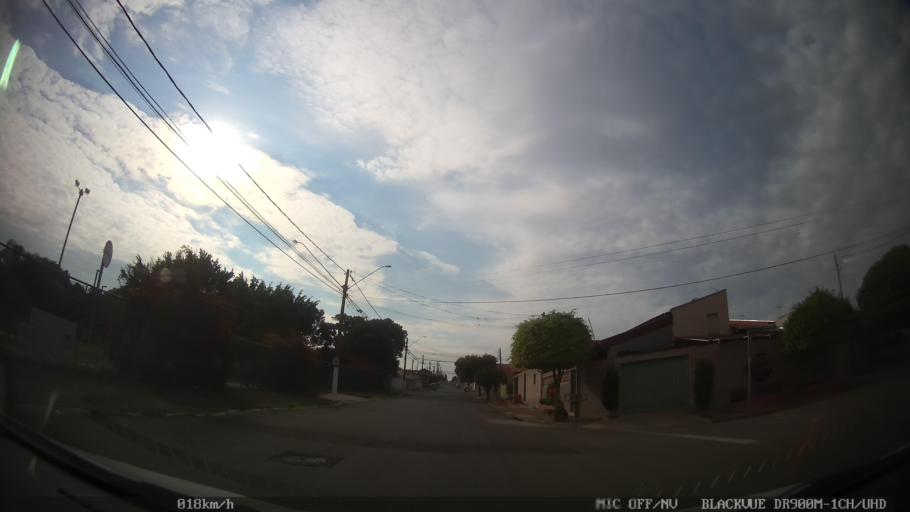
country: BR
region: Sao Paulo
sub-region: Americana
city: Americana
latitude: -22.7515
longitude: -47.3674
